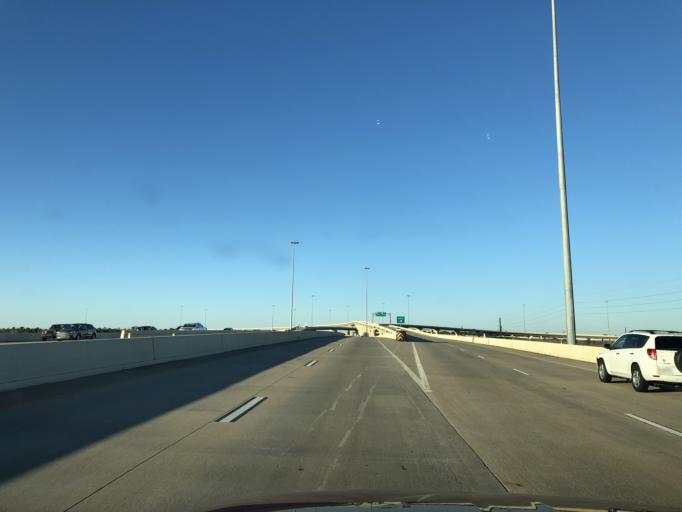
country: US
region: Texas
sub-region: Harris County
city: Cypress
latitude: 29.9912
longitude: -95.7689
